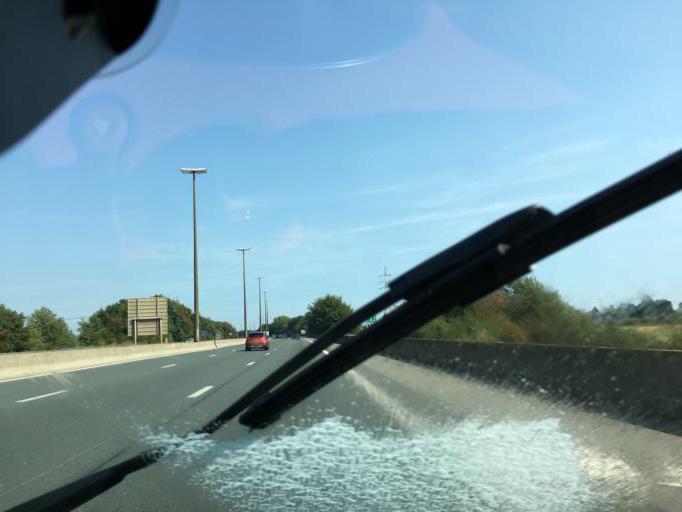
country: BE
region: Wallonia
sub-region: Province du Hainaut
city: Fleurus
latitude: 50.4697
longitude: 4.5086
